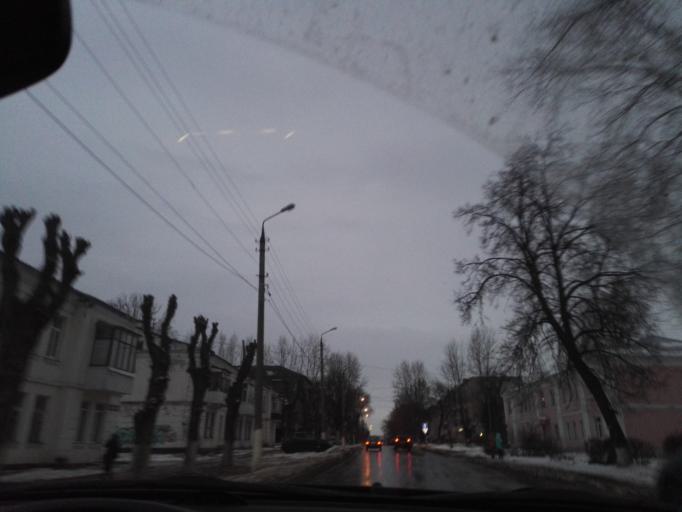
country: RU
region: Tula
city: Novomoskovsk
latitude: 54.0082
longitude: 38.3004
